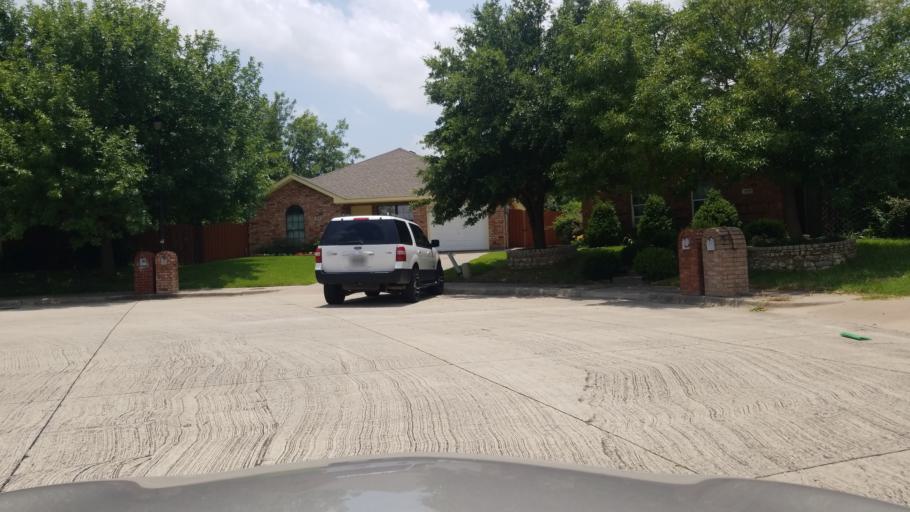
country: US
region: Texas
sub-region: Dallas County
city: Duncanville
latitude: 32.6842
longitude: -96.9092
